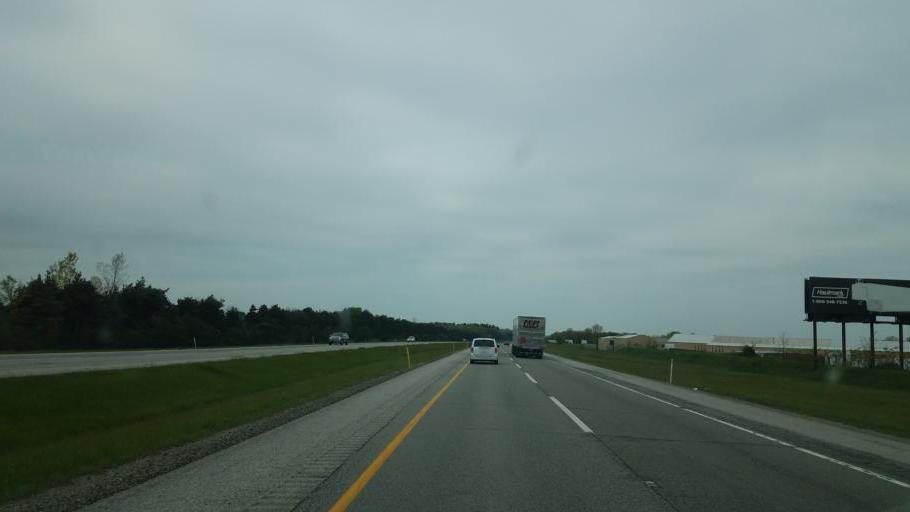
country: US
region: Indiana
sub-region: Elkhart County
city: Middlebury
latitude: 41.7395
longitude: -85.7343
